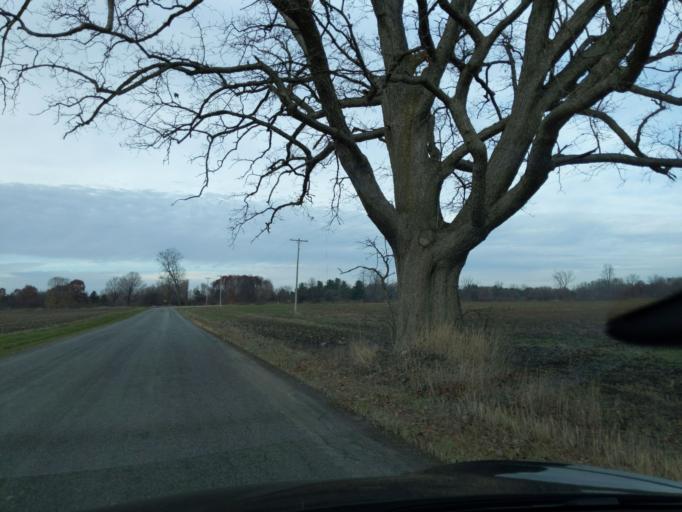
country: US
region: Michigan
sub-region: Ingham County
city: Okemos
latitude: 42.6709
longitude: -84.3834
